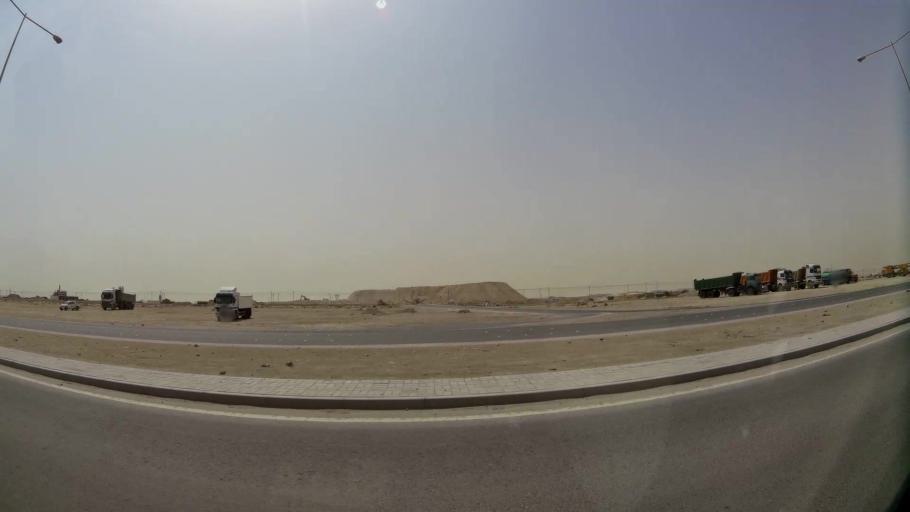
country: QA
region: Baladiyat ar Rayyan
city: Ar Rayyan
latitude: 25.1795
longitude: 51.4048
